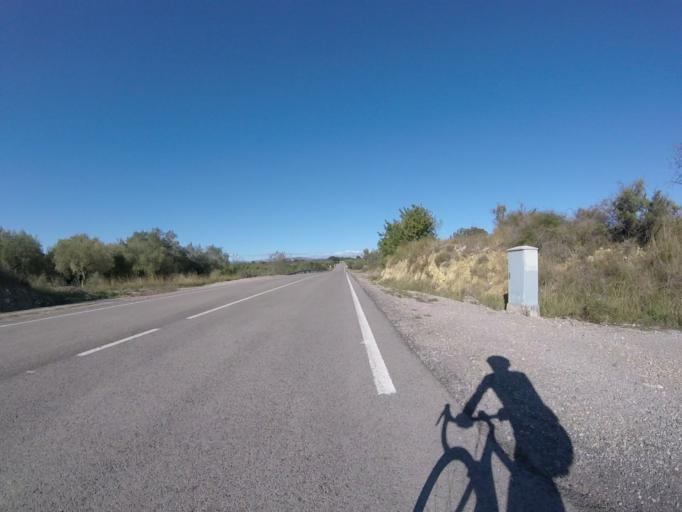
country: ES
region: Valencia
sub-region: Provincia de Castello
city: Cervera del Maestre
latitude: 40.4726
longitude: 0.2382
